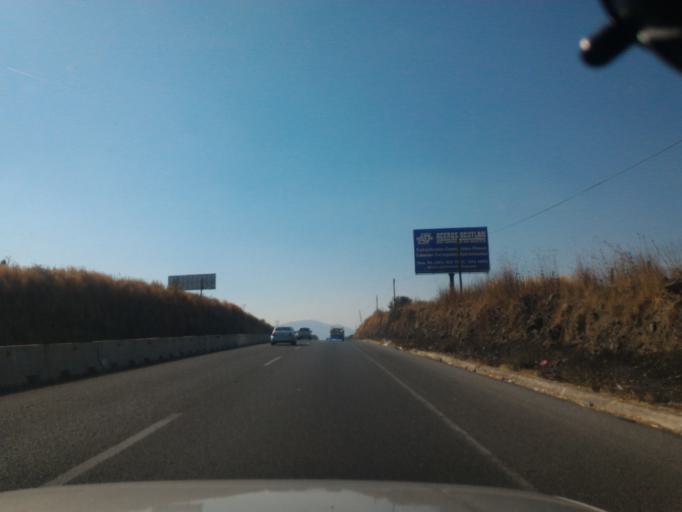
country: MX
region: Jalisco
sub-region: Poncitlan
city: Cuitzeo (La Estancia)
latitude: 20.3653
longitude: -102.8190
